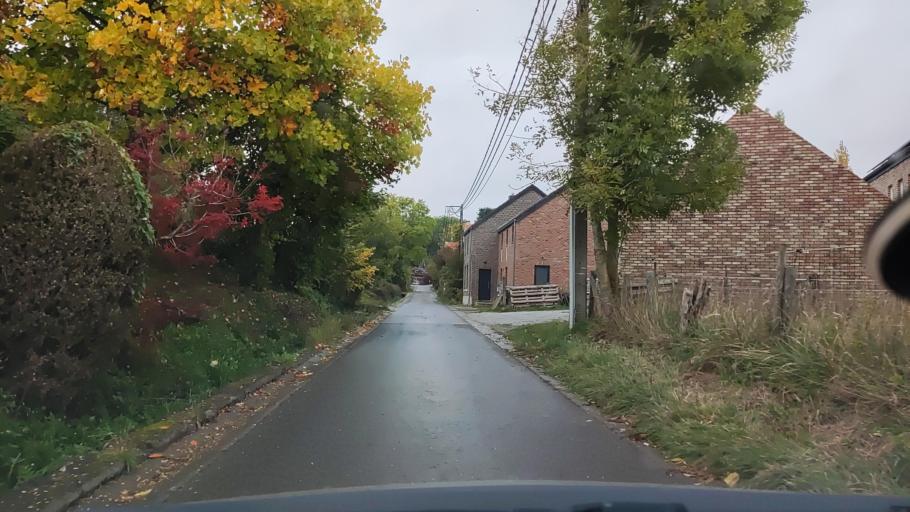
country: BE
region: Wallonia
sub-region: Province du Brabant Wallon
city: Jodoigne
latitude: 50.7503
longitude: 4.8674
